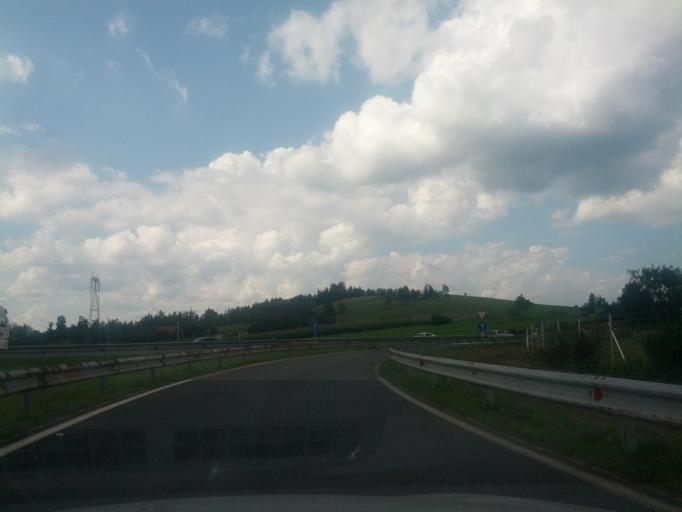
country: SI
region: Cerknica
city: Rakek
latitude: 45.8244
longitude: 14.2885
